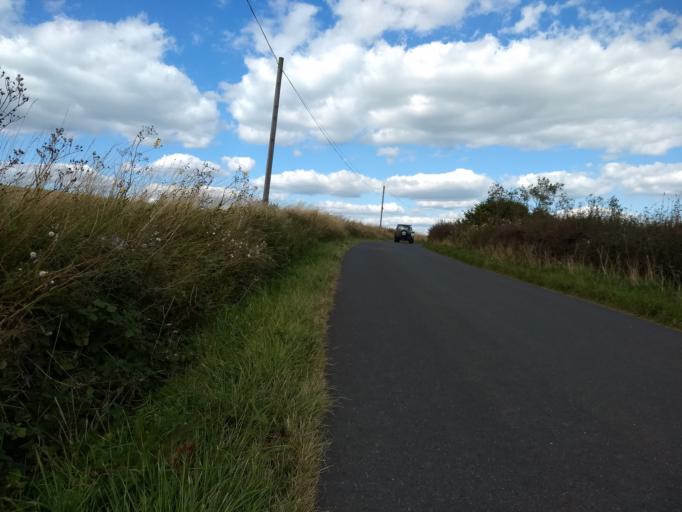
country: GB
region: England
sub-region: Isle of Wight
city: Shalfleet
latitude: 50.6729
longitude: -1.4386
